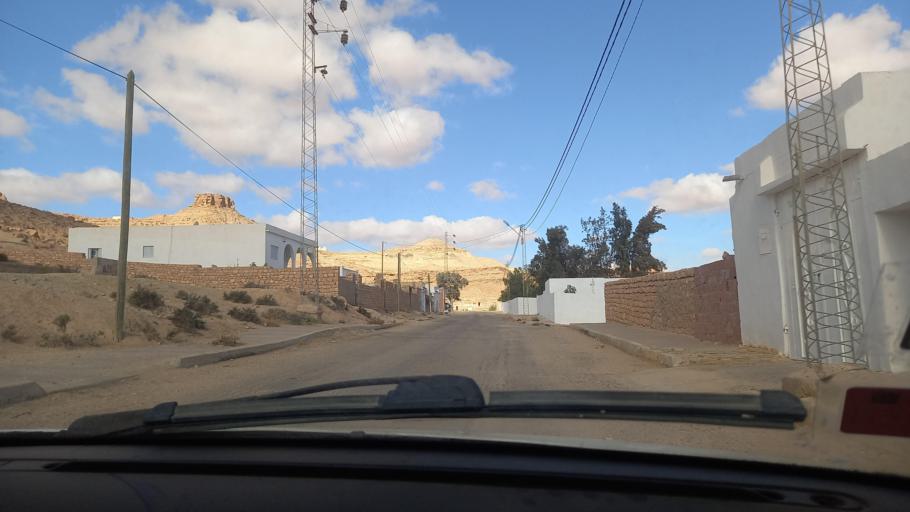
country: TN
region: Tataouine
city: Tataouine
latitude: 32.9830
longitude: 10.2626
